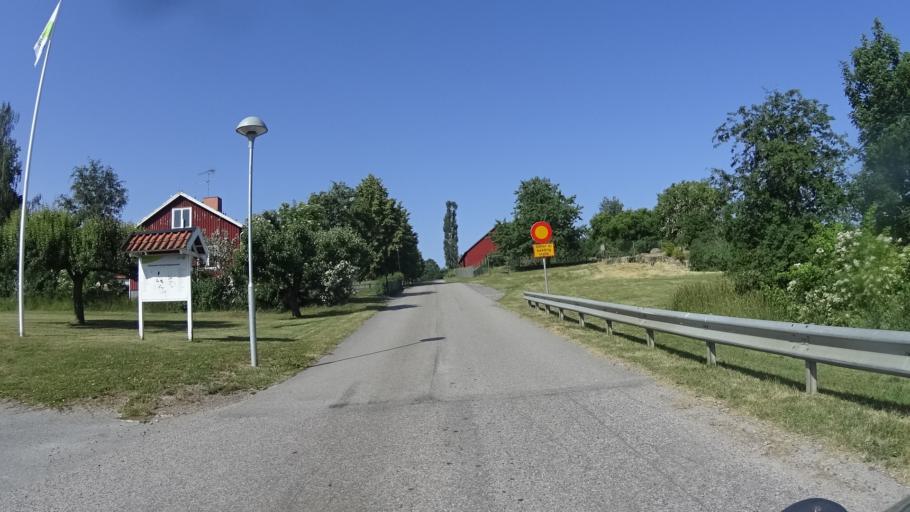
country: SE
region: Kalmar
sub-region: Vasterviks Kommun
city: Gamleby
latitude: 57.9131
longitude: 16.4092
